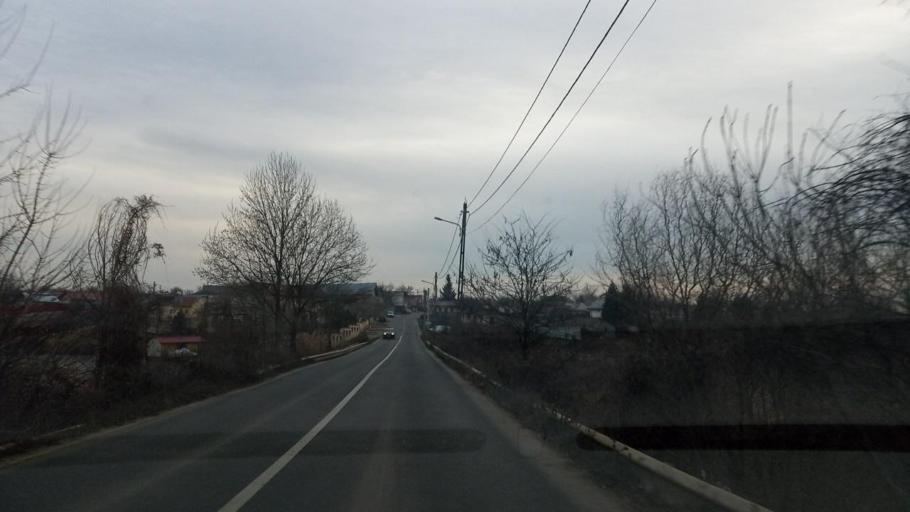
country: RO
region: Ilfov
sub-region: Comuna Ganeasa
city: Ganeasa
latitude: 44.4780
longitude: 26.2955
